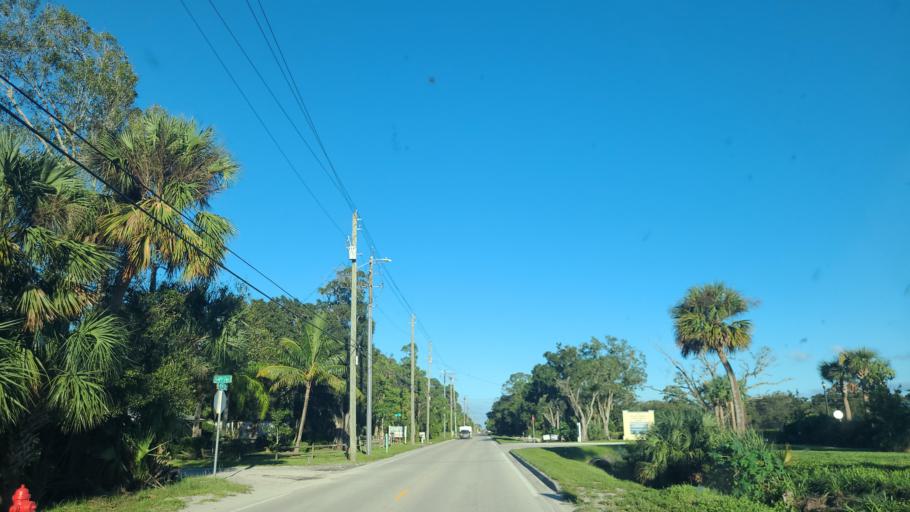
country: US
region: Florida
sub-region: Indian River County
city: Gifford
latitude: 27.6752
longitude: -80.4417
